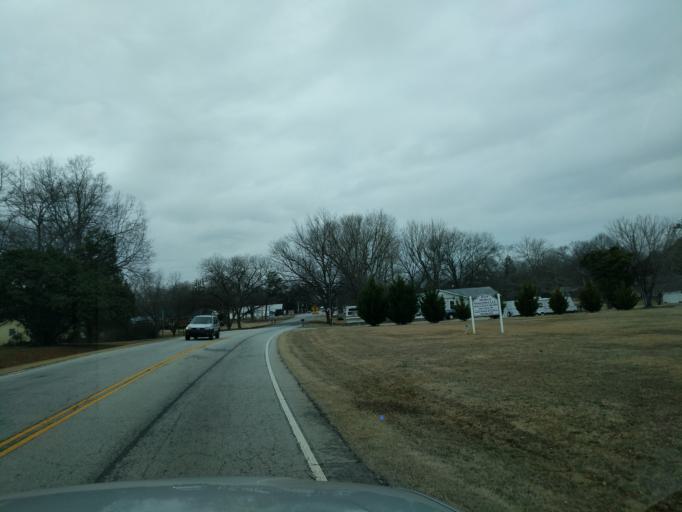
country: US
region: South Carolina
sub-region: Spartanburg County
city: Duncan
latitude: 34.8633
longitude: -82.1104
